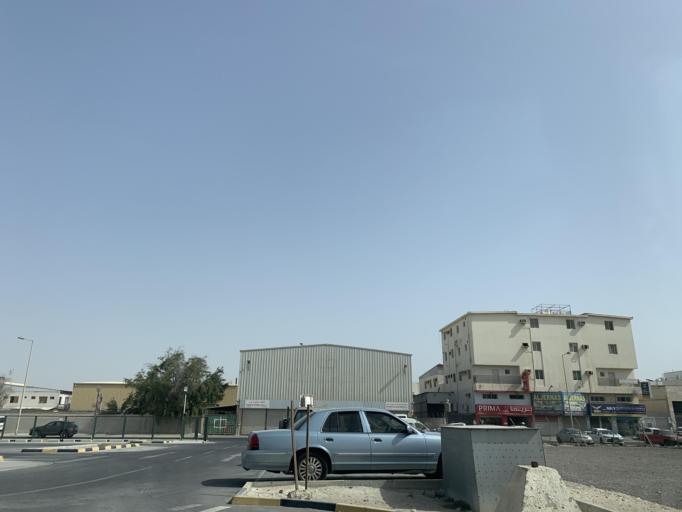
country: BH
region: Northern
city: Madinat `Isa
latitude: 26.1755
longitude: 50.5329
